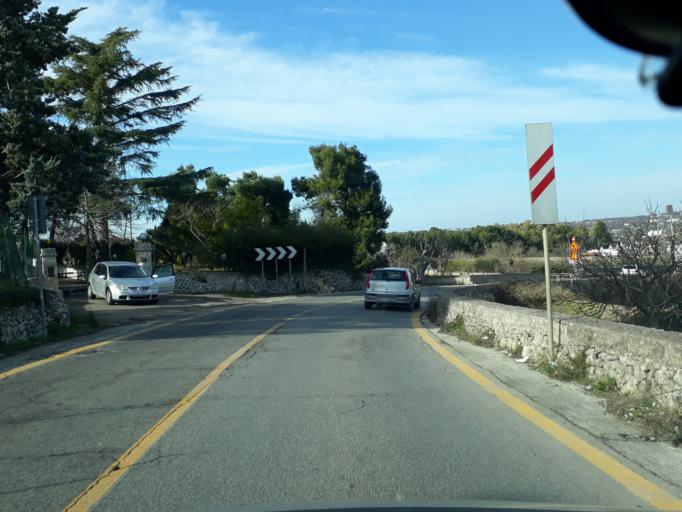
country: IT
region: Apulia
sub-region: Provincia di Taranto
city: Martina Franca
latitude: 40.7127
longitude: 17.3331
